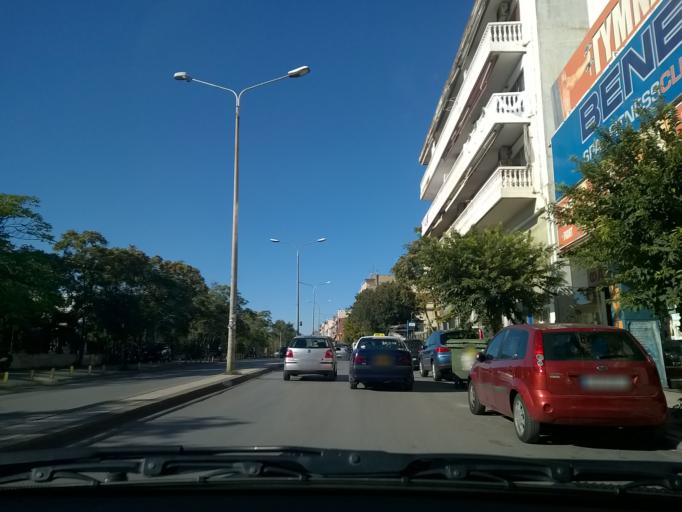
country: GR
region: Central Macedonia
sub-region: Nomos Thessalonikis
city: Thessaloniki
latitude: 40.6512
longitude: 22.9354
